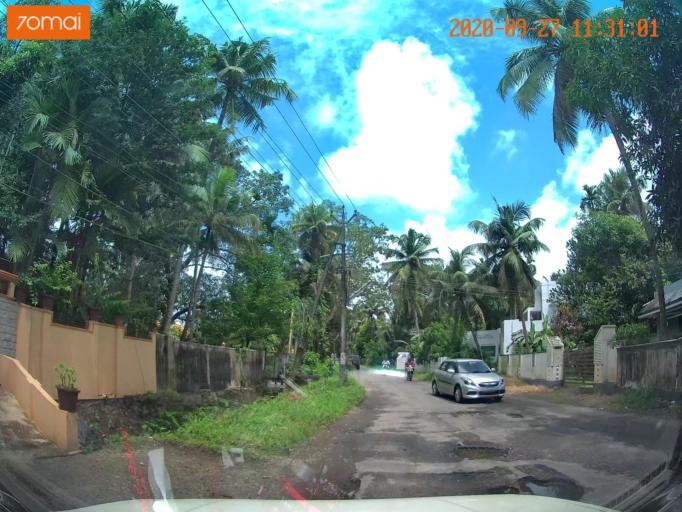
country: IN
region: Kerala
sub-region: Thrissur District
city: Thanniyam
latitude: 10.4211
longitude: 76.1336
